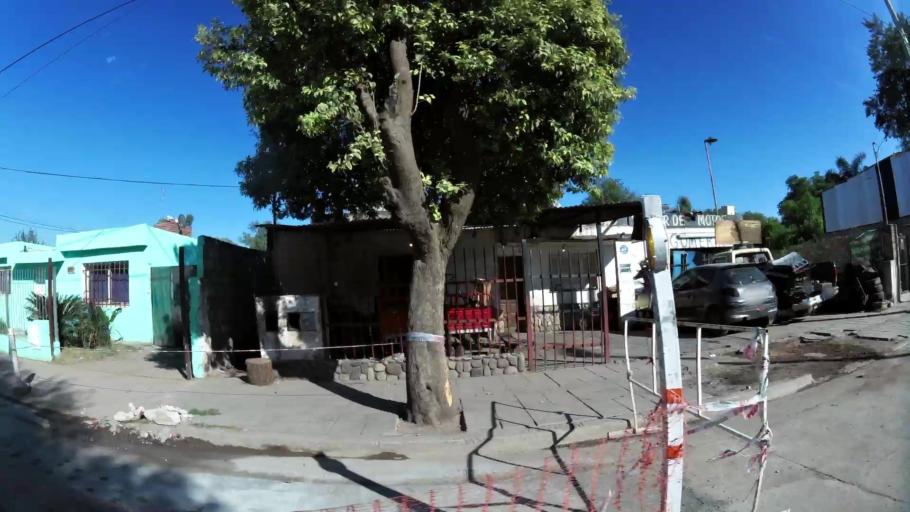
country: AR
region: Cordoba
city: Villa Allende
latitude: -31.3276
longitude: -64.2608
